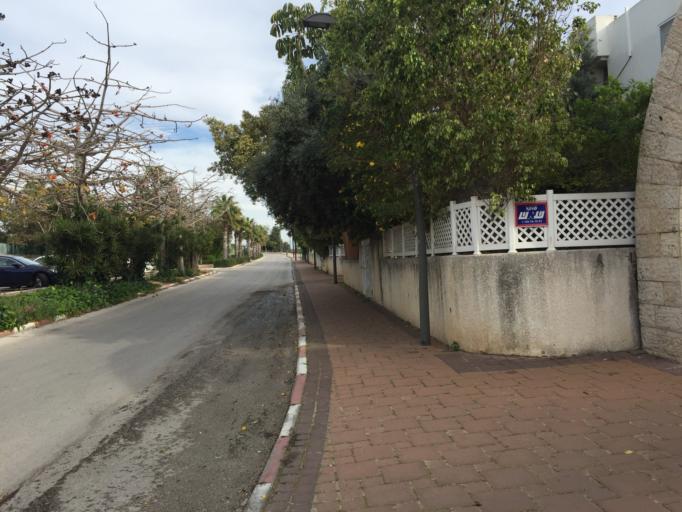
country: IL
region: Haifa
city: Qesarya
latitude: 32.5121
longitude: 34.9031
